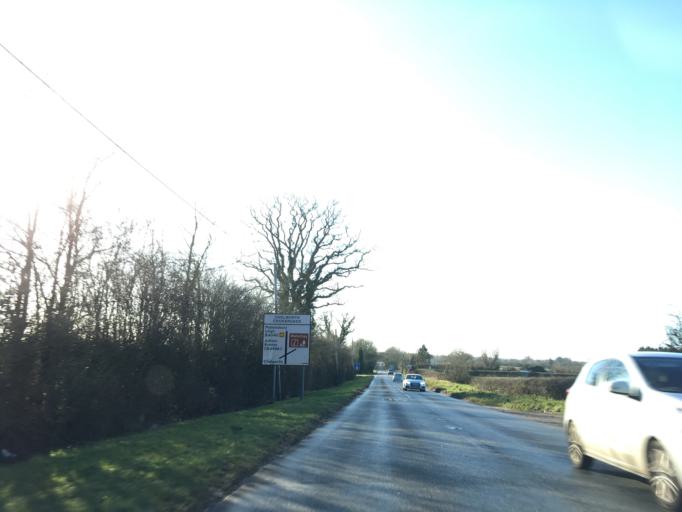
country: GB
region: England
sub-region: Wiltshire
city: Leigh
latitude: 51.6358
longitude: -1.8840
